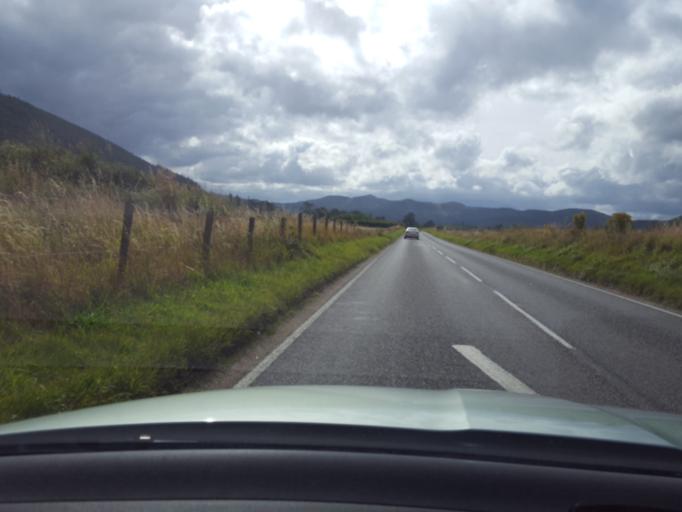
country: GB
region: Scotland
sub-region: Aberdeenshire
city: Ballater
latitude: 57.0597
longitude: -3.0200
